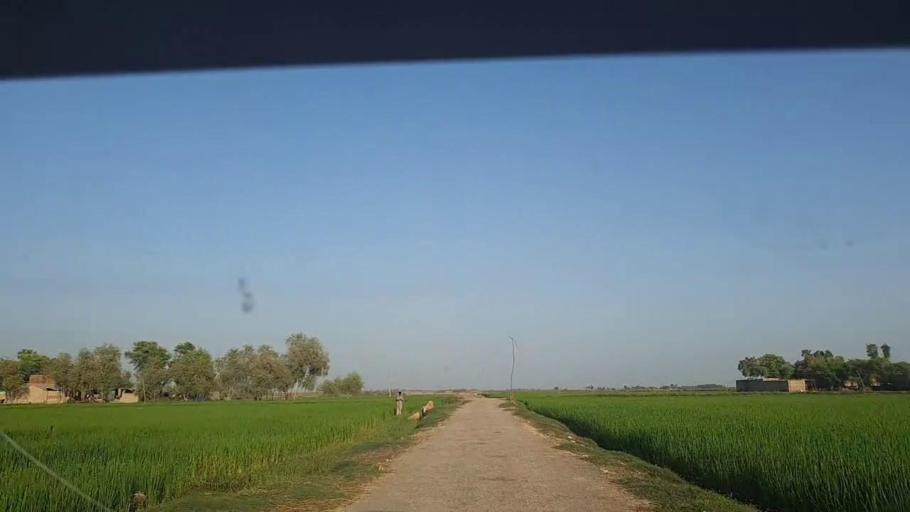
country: PK
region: Sindh
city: Thul
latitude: 28.2118
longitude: 68.8849
